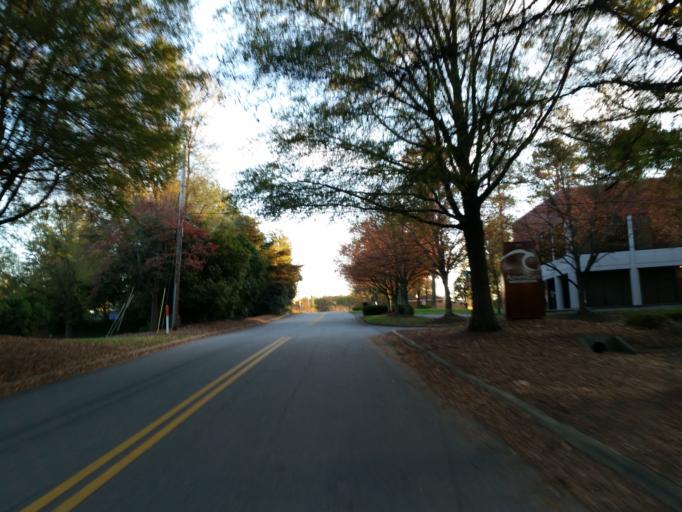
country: US
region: Georgia
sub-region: Cobb County
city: Marietta
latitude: 33.9420
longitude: -84.5101
